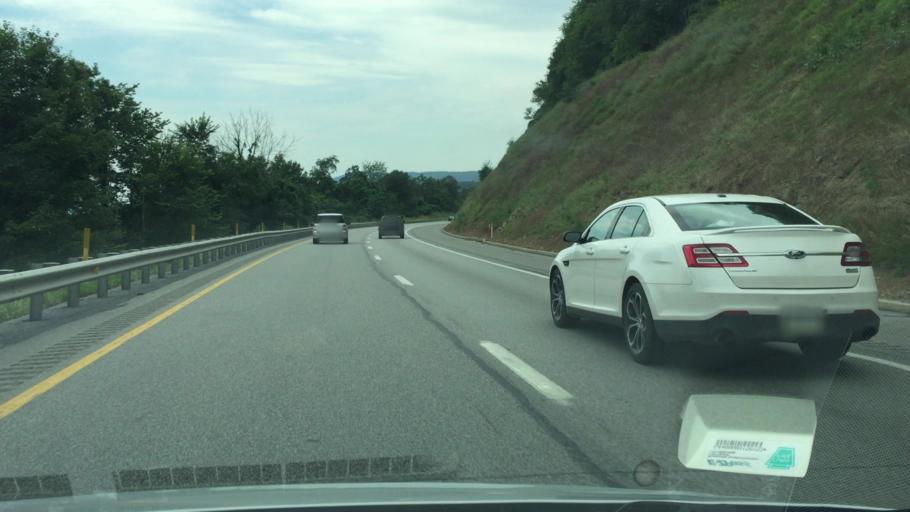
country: US
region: Pennsylvania
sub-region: Bedford County
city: Earlston
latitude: 39.8721
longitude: -78.2530
